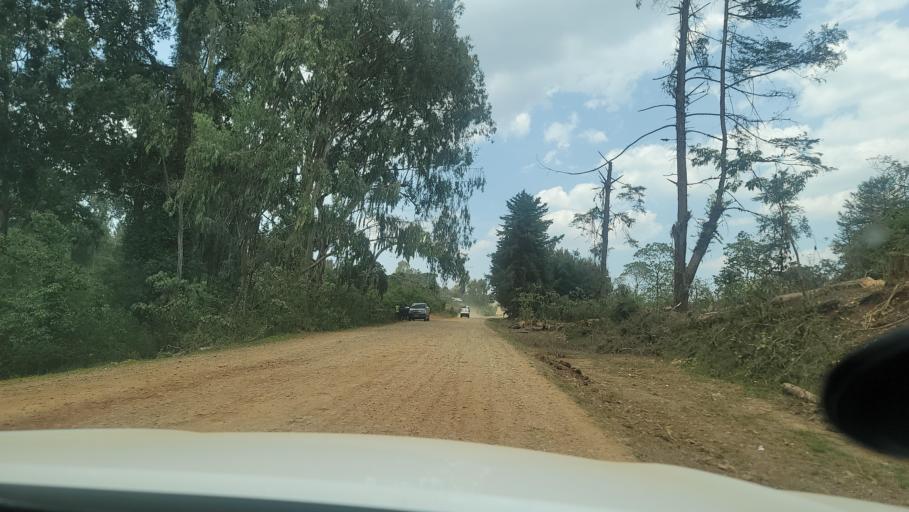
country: ET
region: Oromiya
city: Agaro
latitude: 7.7931
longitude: 36.4367
